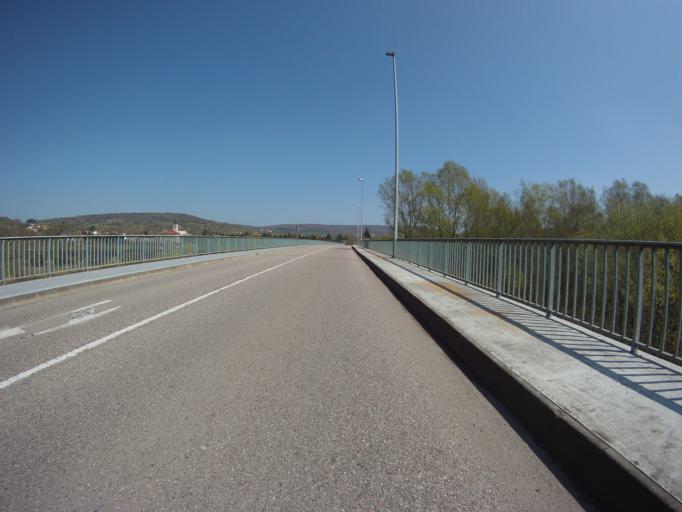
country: FR
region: Lorraine
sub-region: Departement de Meurthe-et-Moselle
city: Custines
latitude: 48.7886
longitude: 6.1392
